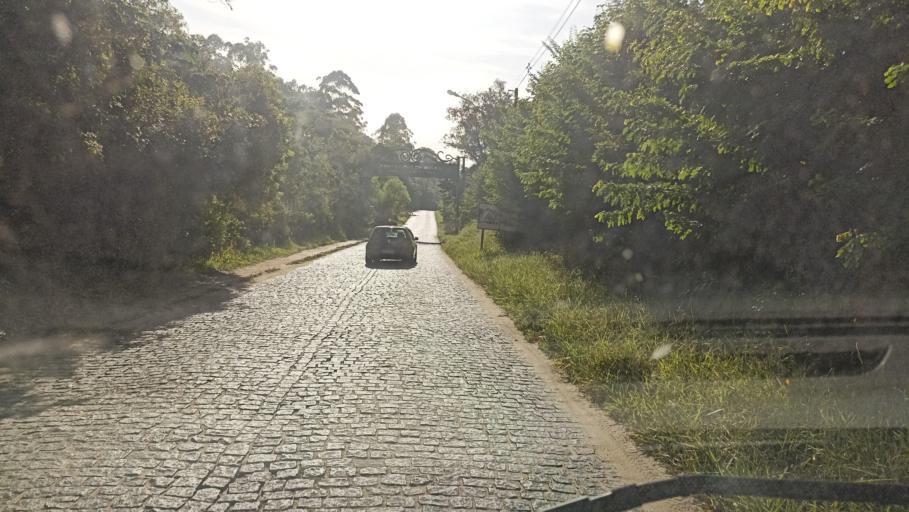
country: BR
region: Minas Gerais
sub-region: Tiradentes
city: Tiradentes
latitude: -21.1195
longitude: -44.2005
